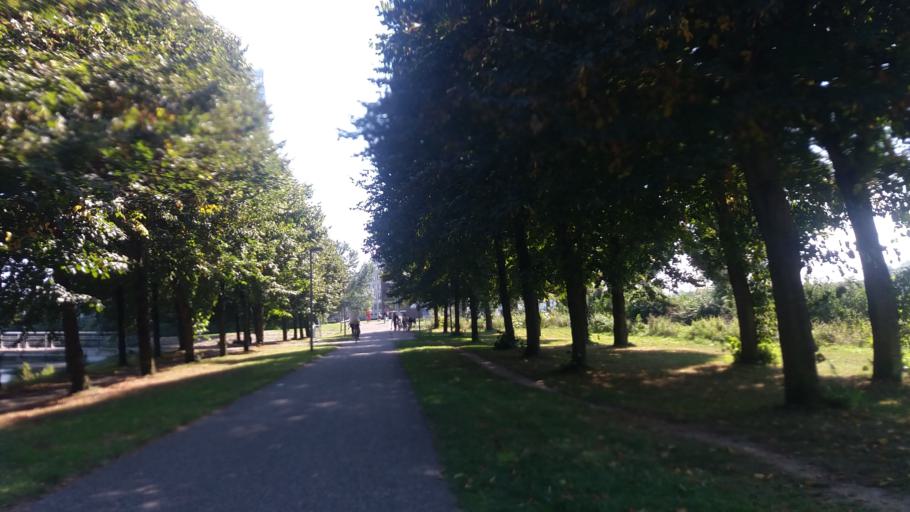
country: NL
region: Flevoland
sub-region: Gemeente Almere
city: Almere Stad
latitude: 52.3628
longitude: 5.2357
